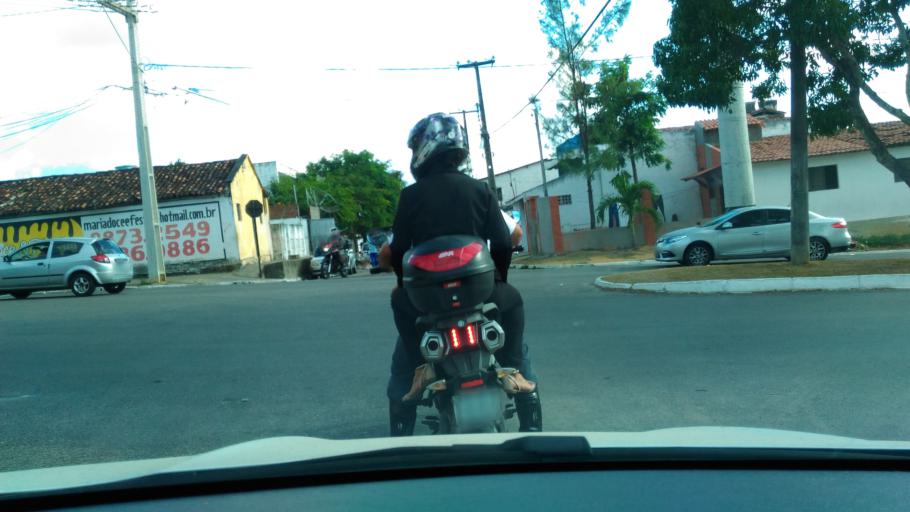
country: BR
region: Paraiba
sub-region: Joao Pessoa
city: Joao Pessoa
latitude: -7.1255
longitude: -34.8864
